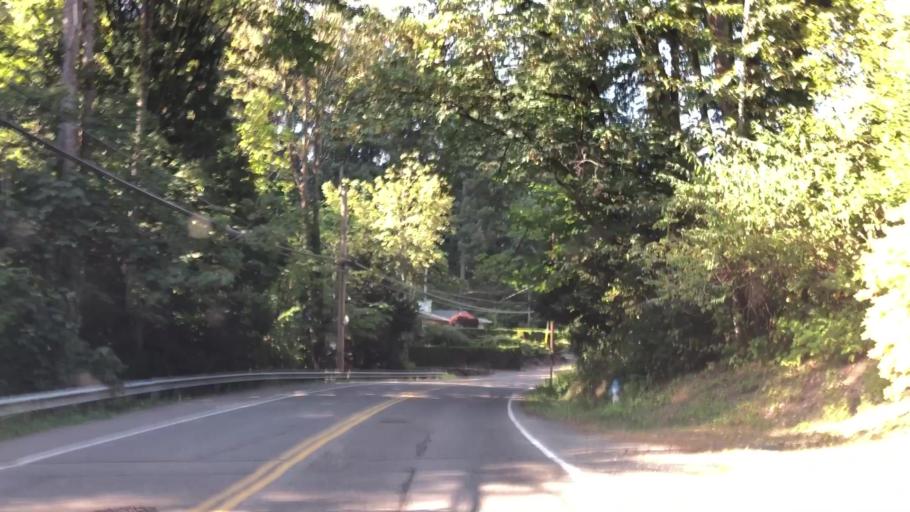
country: US
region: Washington
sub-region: King County
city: Lake Forest Park
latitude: 47.7654
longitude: -122.2851
